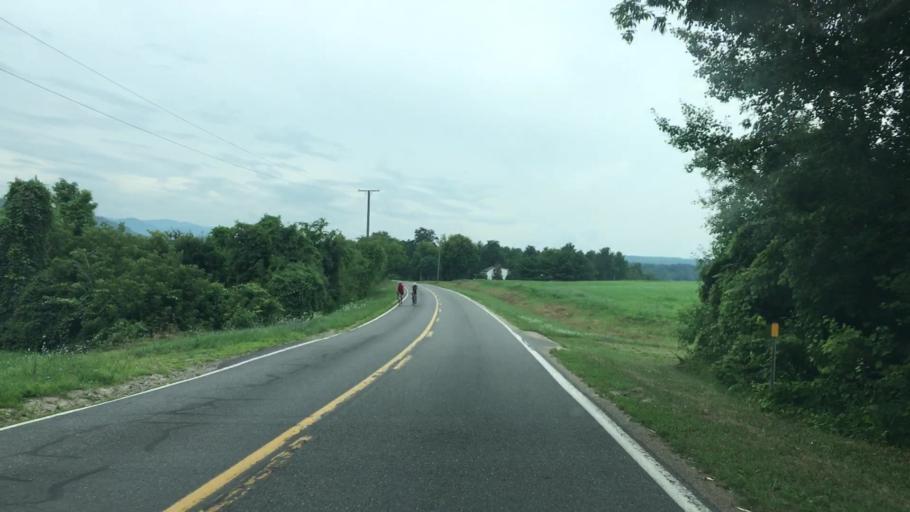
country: US
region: New York
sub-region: Clinton County
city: Peru
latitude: 44.5401
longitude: -73.5699
